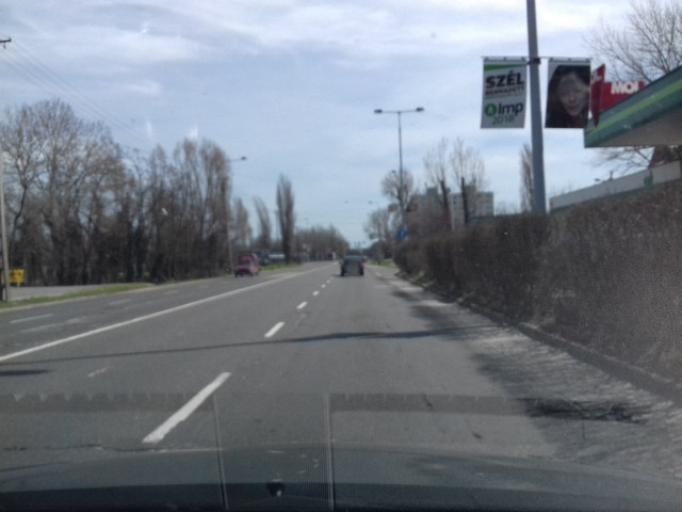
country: HU
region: Bacs-Kiskun
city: Kecskemet
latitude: 46.9224
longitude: 19.6760
